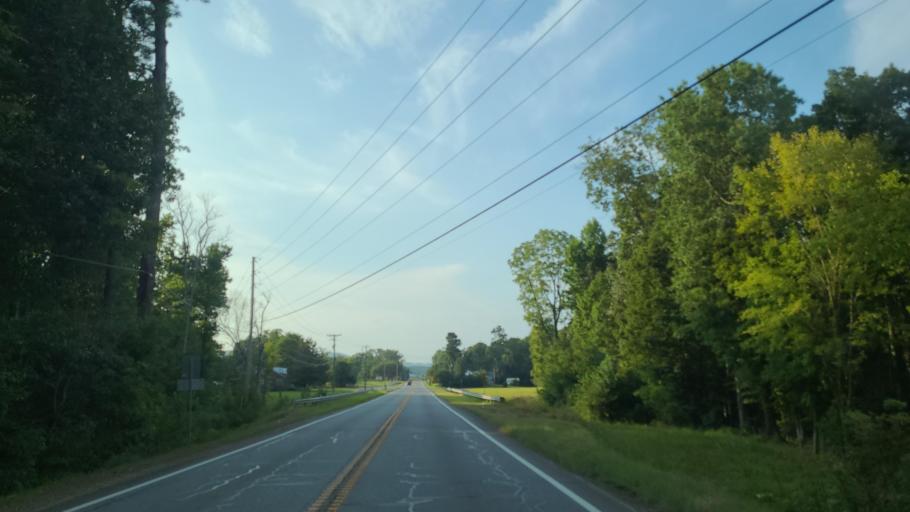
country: US
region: Georgia
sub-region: Whitfield County
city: Dalton
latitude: 34.6779
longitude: -84.9846
